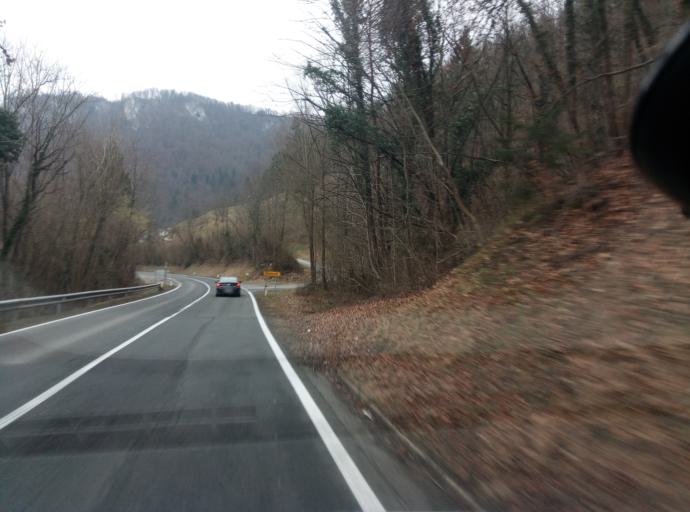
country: SI
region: Zagorje ob Savi
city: Kisovec
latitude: 46.0917
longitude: 14.9445
